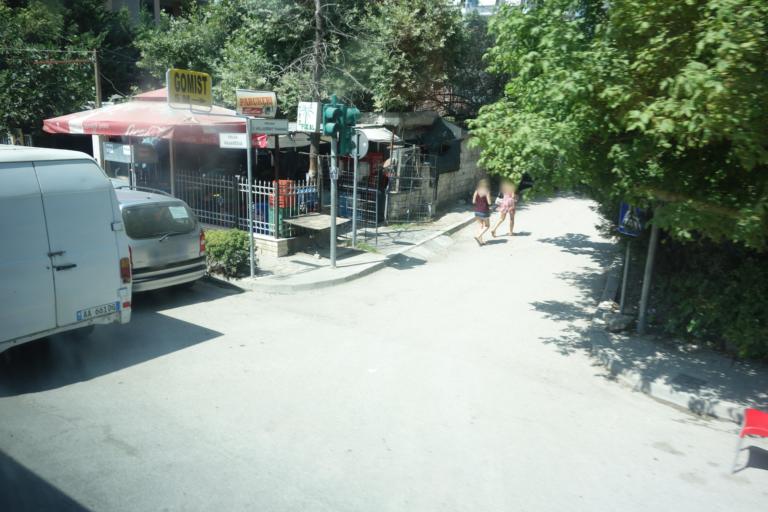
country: AL
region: Durres
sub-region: Rrethi i Durresit
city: Rrashbull
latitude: 41.3090
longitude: 19.4873
